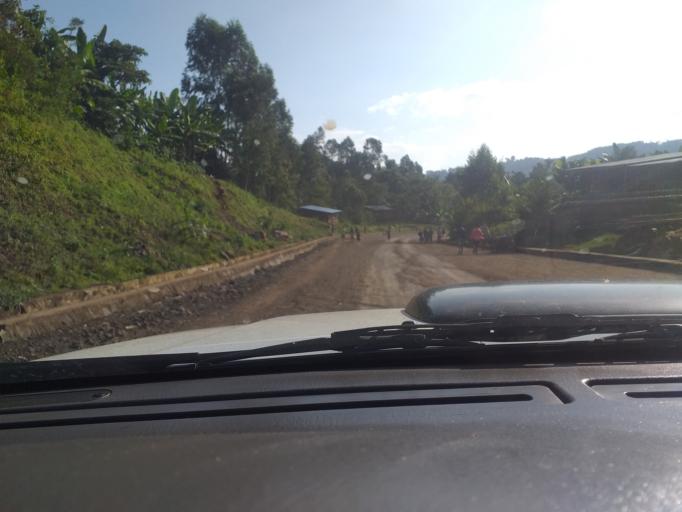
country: ET
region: Southern Nations, Nationalities, and People's Region
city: Bako
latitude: 5.9798
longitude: 36.5729
